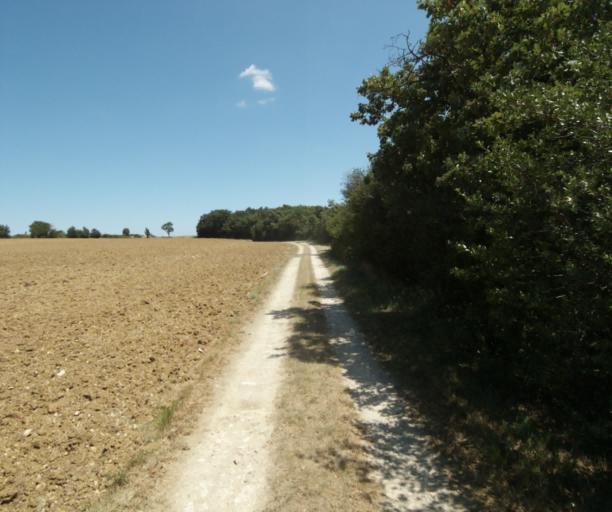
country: FR
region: Midi-Pyrenees
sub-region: Departement de la Haute-Garonne
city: Auriac-sur-Vendinelle
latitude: 43.4872
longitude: 1.8538
